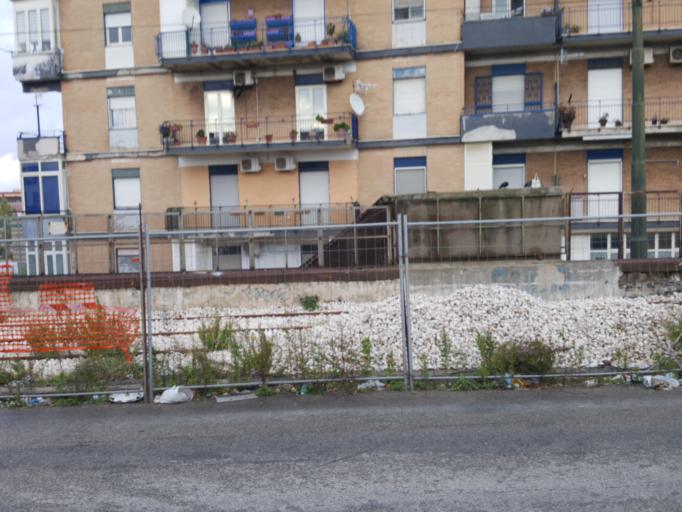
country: IT
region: Campania
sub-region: Provincia di Napoli
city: San Giorgio a Cremano
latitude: 40.8394
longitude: 14.2957
